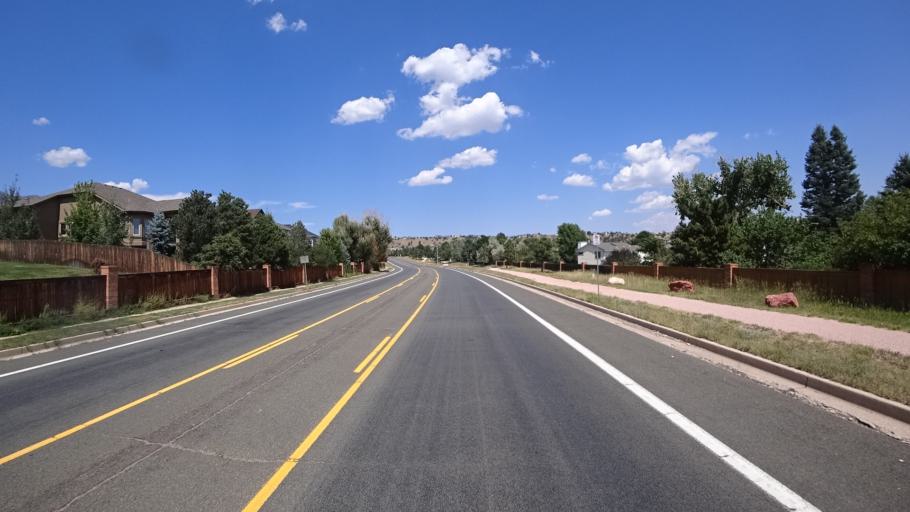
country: US
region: Colorado
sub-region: El Paso County
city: Air Force Academy
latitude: 38.9229
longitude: -104.8672
